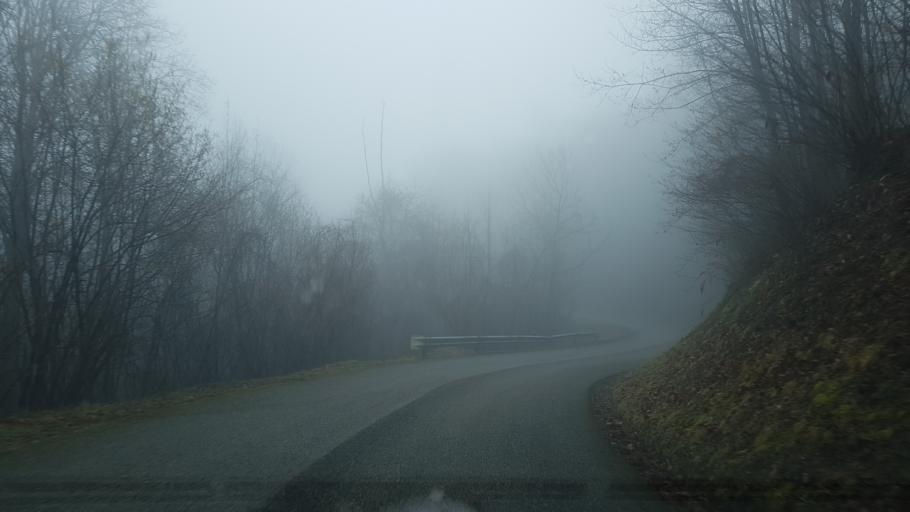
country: IT
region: Friuli Venezia Giulia
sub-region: Provincia di Udine
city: Stregna
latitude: 46.1200
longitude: 13.5968
